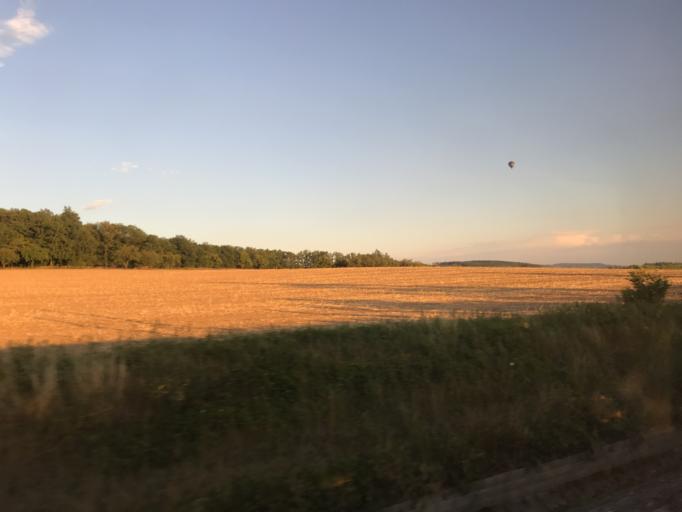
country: CZ
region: Central Bohemia
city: Bystrice
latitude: 49.7465
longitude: 14.6773
